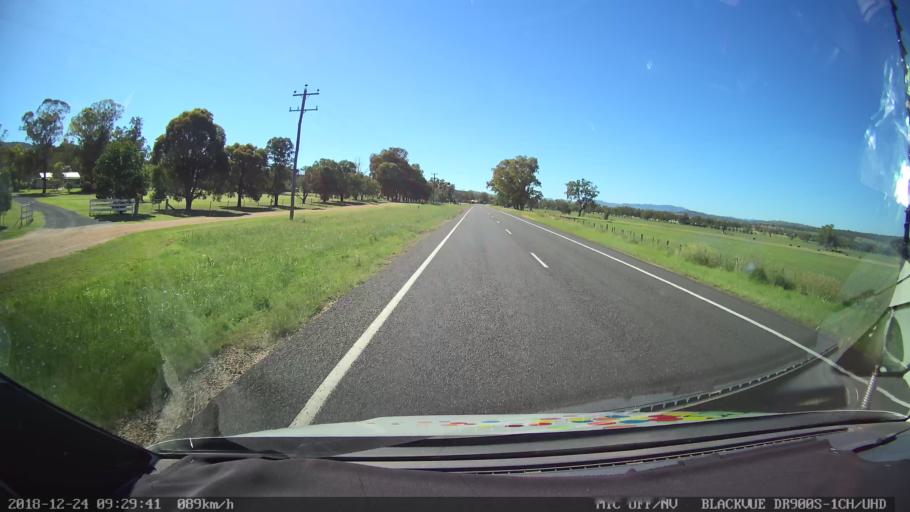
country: AU
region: New South Wales
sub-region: Liverpool Plains
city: Quirindi
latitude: -31.5538
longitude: 150.6929
